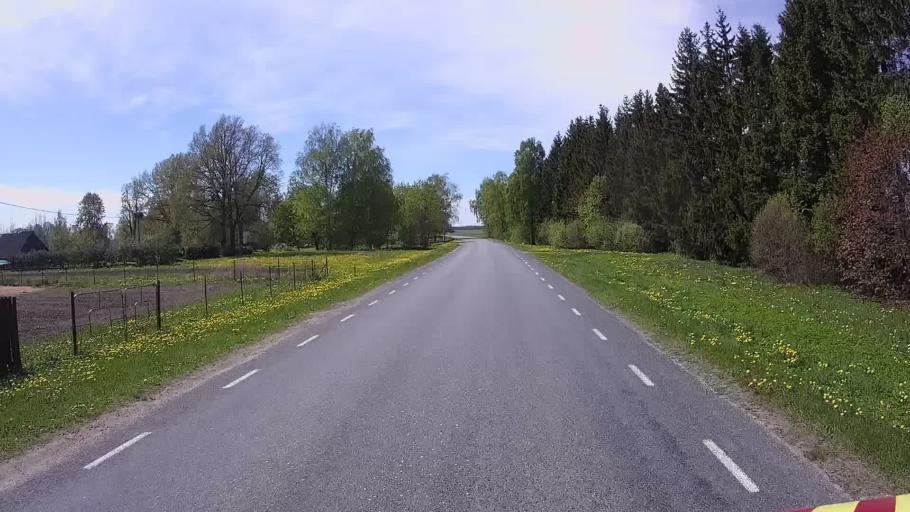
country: LV
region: Apes Novads
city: Ape
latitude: 57.6070
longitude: 26.5576
